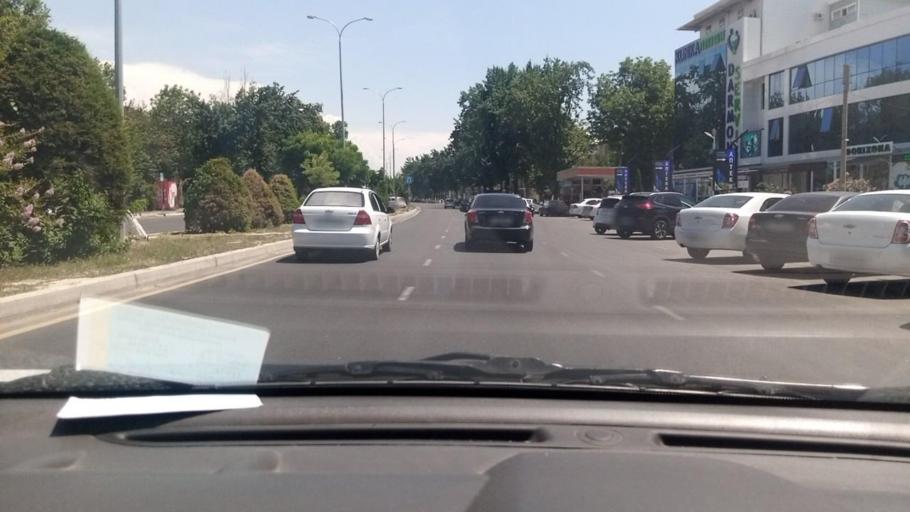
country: UZ
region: Toshkent Shahri
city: Tashkent
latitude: 41.2889
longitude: 69.2019
